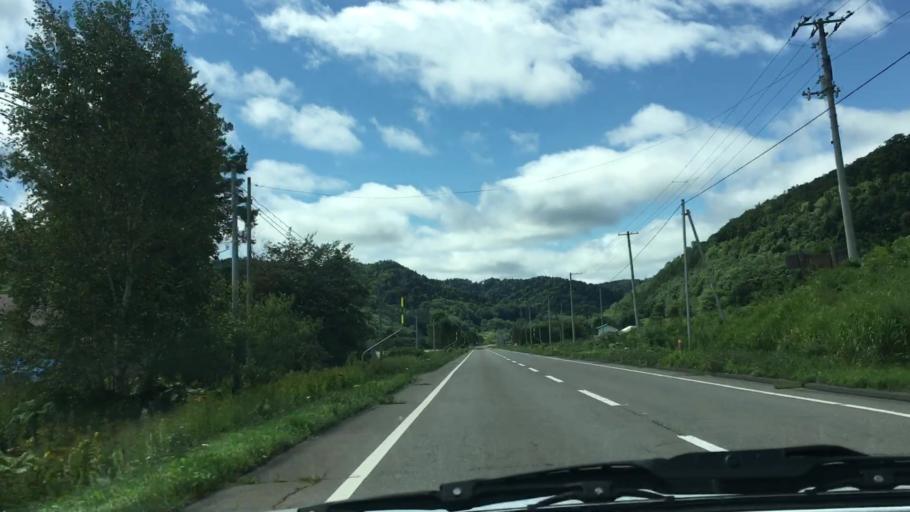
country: JP
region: Hokkaido
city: Kitami
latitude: 43.3664
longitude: 143.8595
